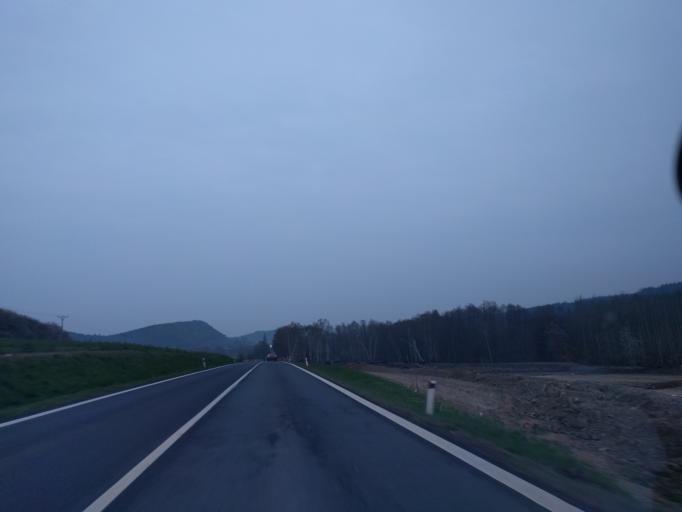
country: CZ
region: Ustecky
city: Lubenec
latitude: 50.1250
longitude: 13.3396
